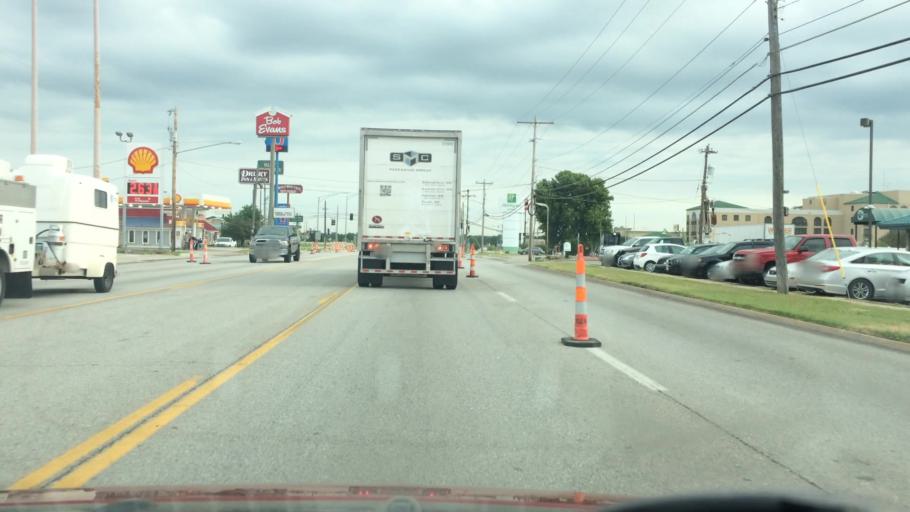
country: US
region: Missouri
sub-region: Greene County
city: Springfield
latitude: 37.2441
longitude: -93.2609
